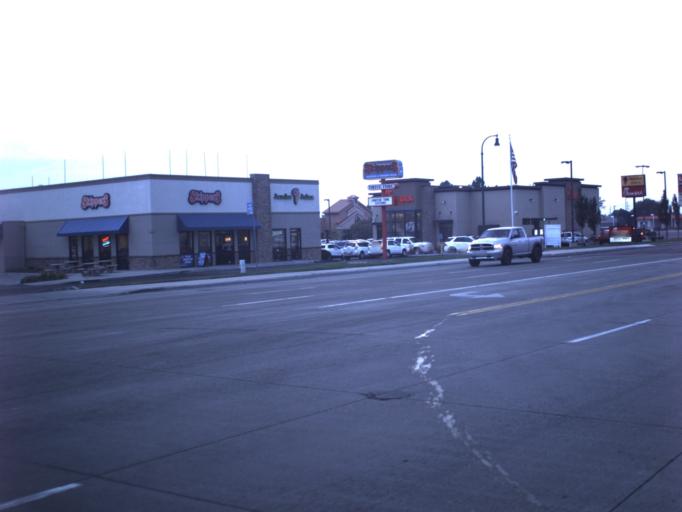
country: US
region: Utah
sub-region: Utah County
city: Orem
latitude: 40.2989
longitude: -111.6957
